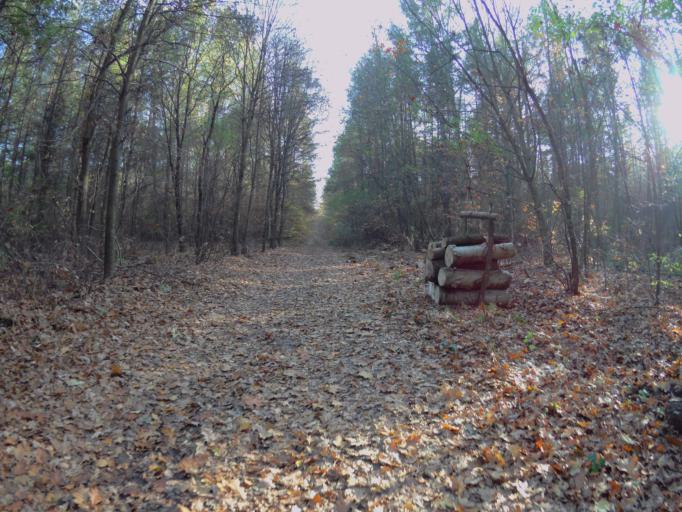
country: PL
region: Subcarpathian Voivodeship
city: Nowa Sarzyna
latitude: 50.3131
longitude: 22.3444
